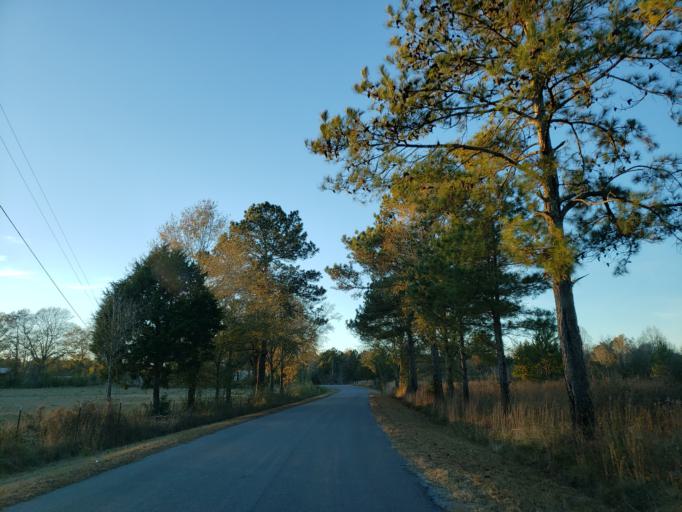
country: US
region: Mississippi
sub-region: Covington County
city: Collins
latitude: 31.5721
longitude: -89.4562
